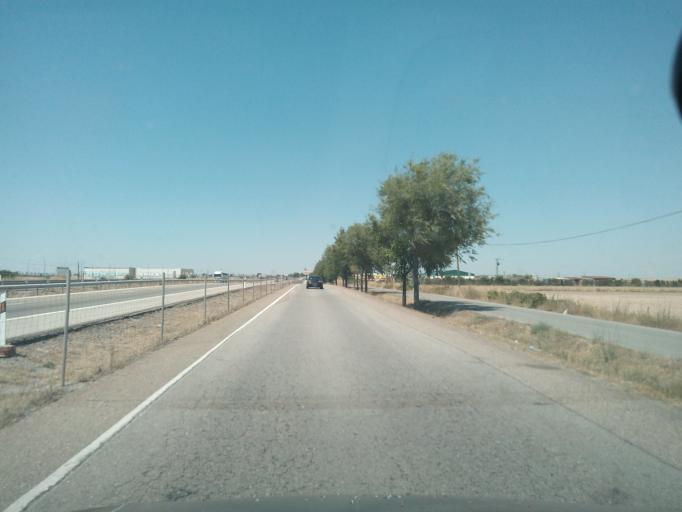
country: ES
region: Castille-La Mancha
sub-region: Province of Toledo
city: Tembleque
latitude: 39.7676
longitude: -3.4802
